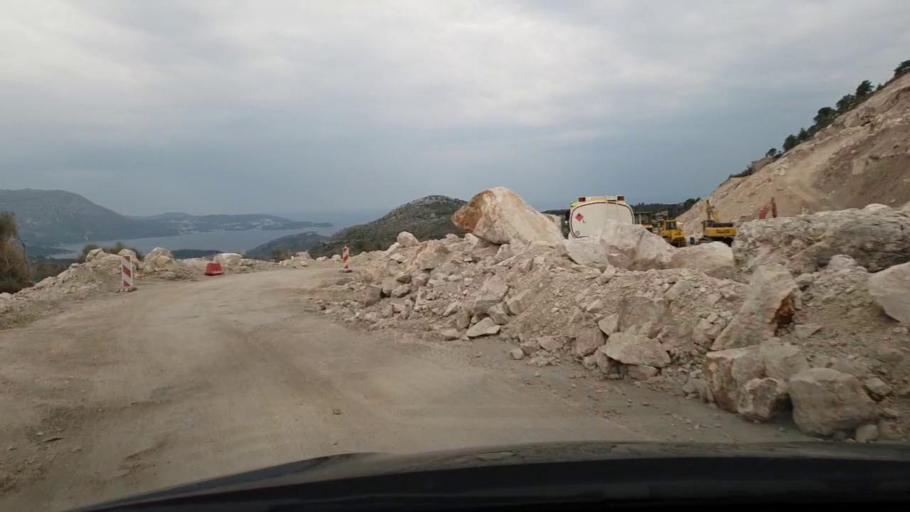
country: HR
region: Dubrovacko-Neretvanska
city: Cibaca
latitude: 42.6526
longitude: 18.1592
